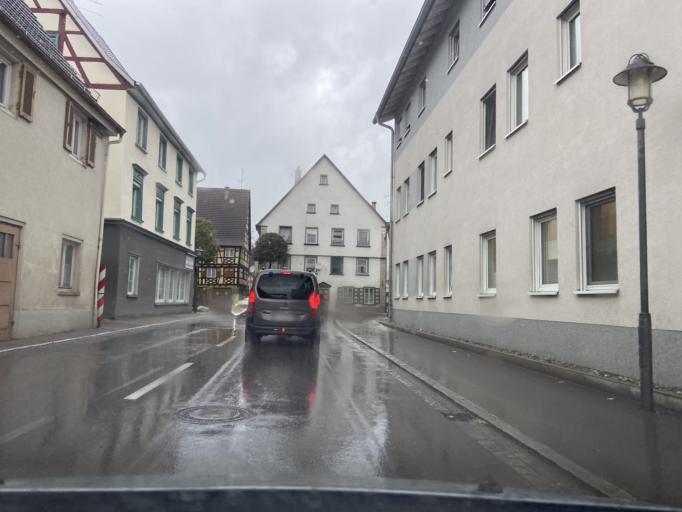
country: DE
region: Baden-Wuerttemberg
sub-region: Tuebingen Region
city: Scheer
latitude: 48.0728
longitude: 9.2942
